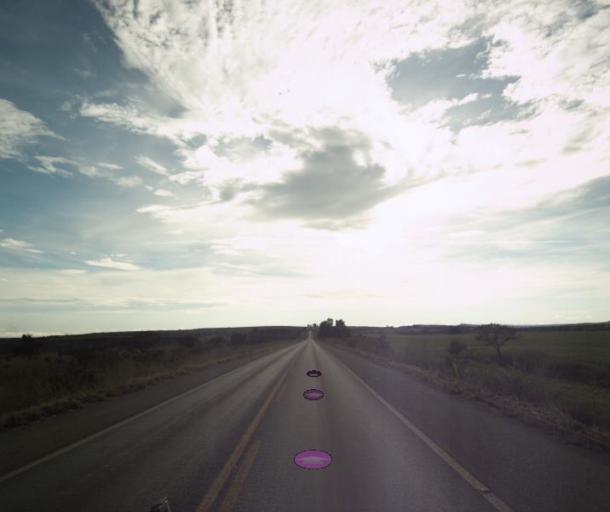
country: BR
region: Goias
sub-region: Pirenopolis
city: Pirenopolis
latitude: -15.7550
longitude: -48.6819
